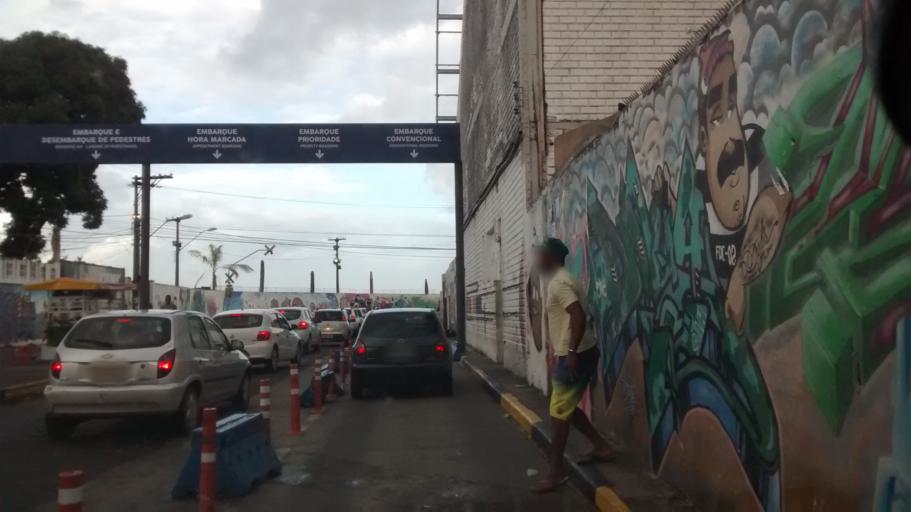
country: BR
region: Bahia
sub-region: Salvador
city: Salvador
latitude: -12.9547
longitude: -38.5024
